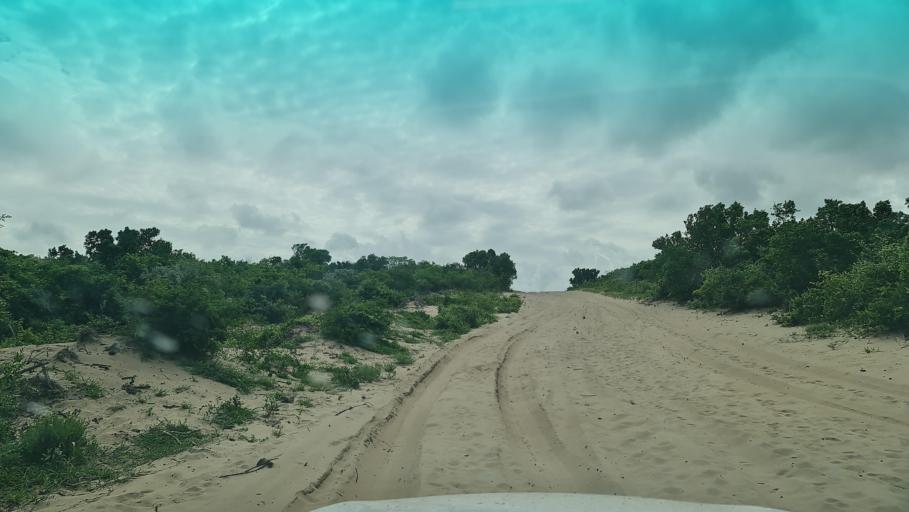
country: MZ
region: Maputo
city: Manhica
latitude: -25.4415
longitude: 32.9410
